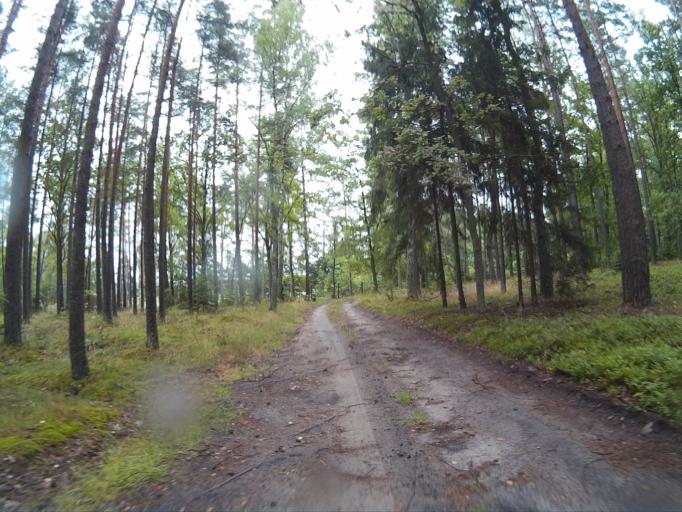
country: PL
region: Kujawsko-Pomorskie
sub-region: Powiat swiecki
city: Osie
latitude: 53.6465
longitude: 18.4176
